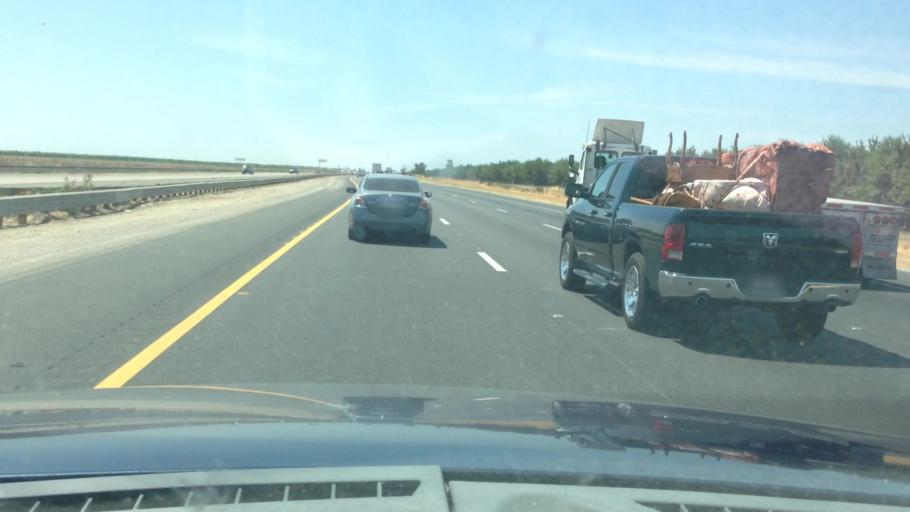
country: US
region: California
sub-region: Kern County
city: McFarland
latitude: 35.6405
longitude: -119.2183
